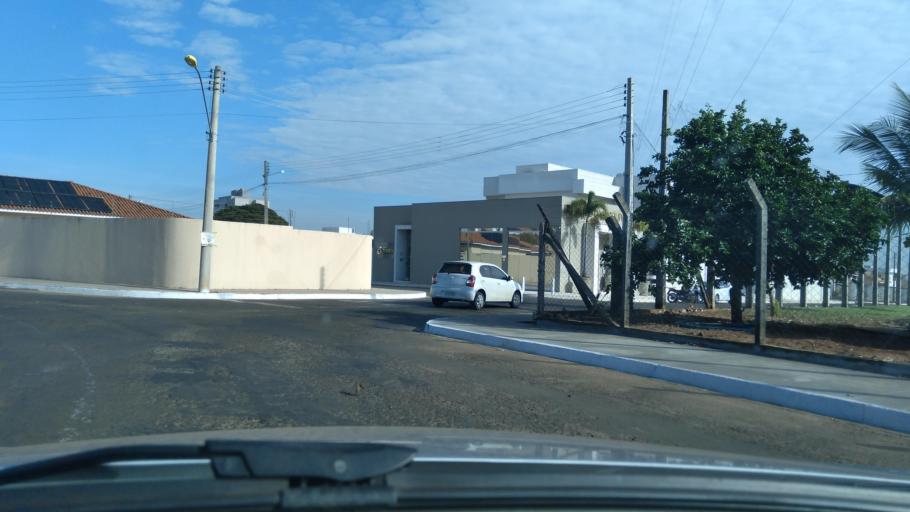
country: BR
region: Goias
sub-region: Mineiros
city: Mineiros
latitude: -17.5586
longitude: -52.5604
